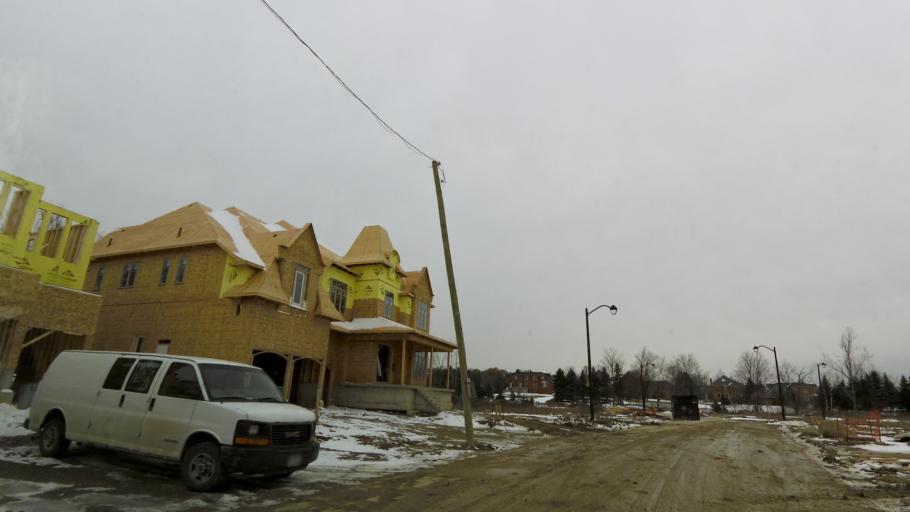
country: CA
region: Ontario
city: Vaughan
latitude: 43.8953
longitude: -79.6608
